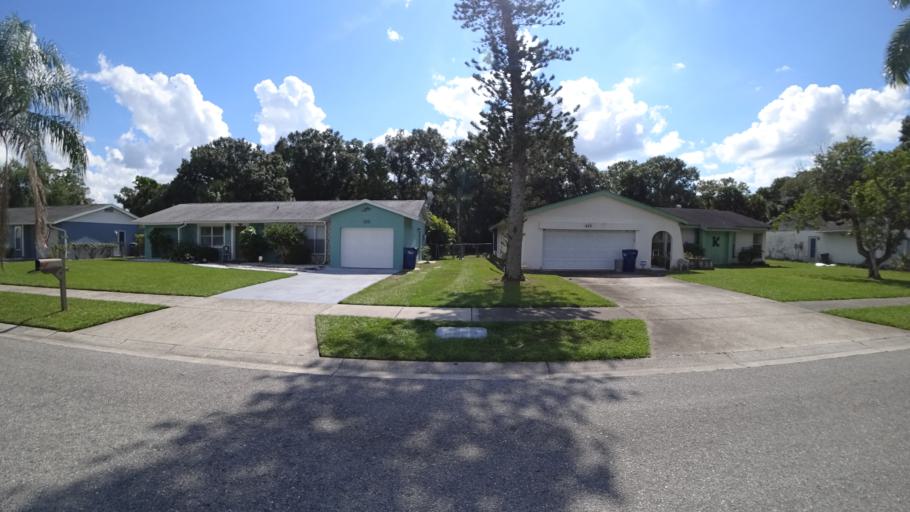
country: US
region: Florida
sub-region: Manatee County
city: Whitfield
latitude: 27.4143
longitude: -82.5582
